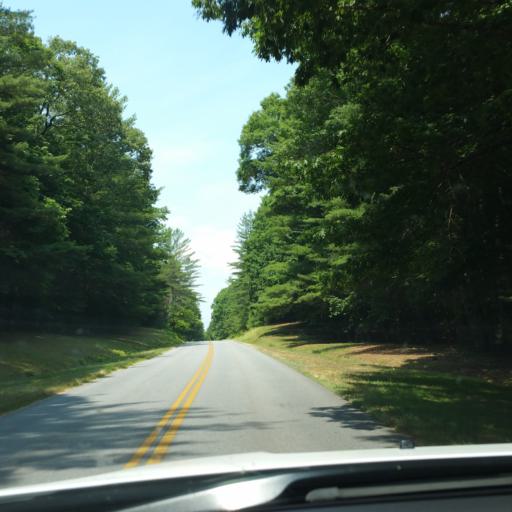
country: US
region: North Carolina
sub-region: Buncombe County
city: Biltmore Forest
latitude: 35.5148
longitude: -82.5419
